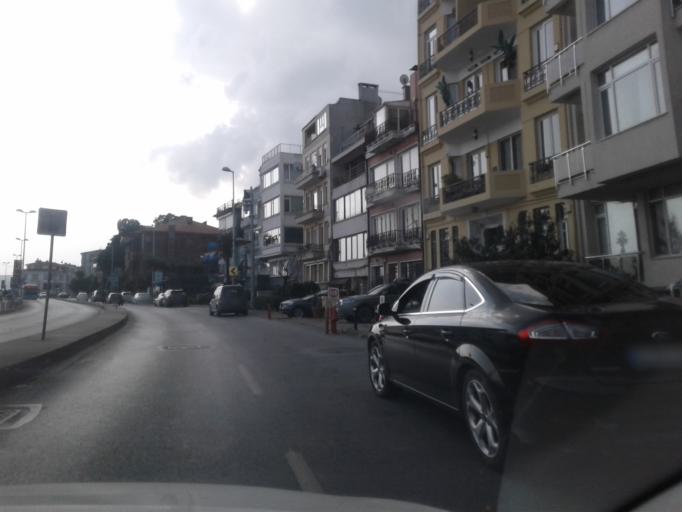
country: TR
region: Istanbul
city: UEskuedar
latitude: 41.0657
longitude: 29.0412
